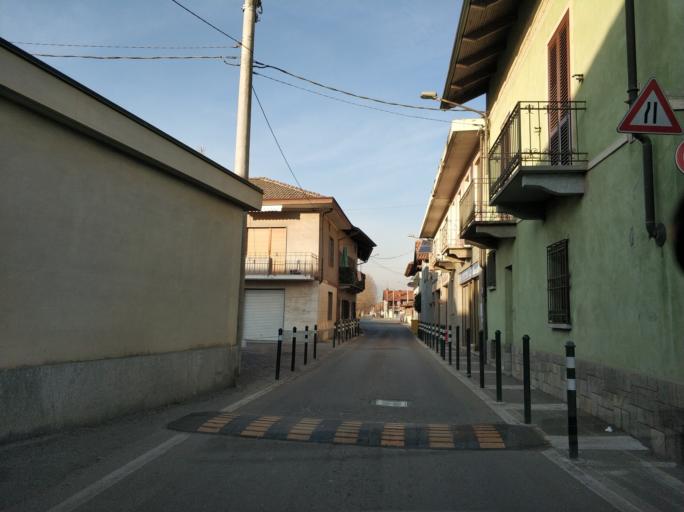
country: IT
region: Piedmont
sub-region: Provincia di Torino
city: San Francesco al Campo
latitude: 45.2030
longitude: 7.6551
